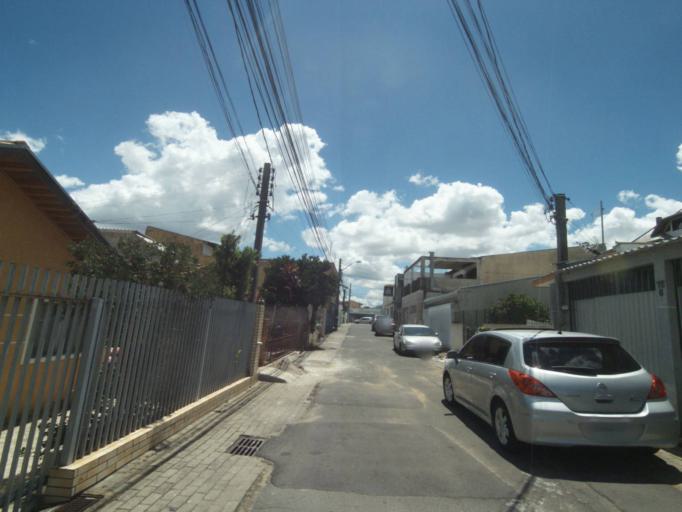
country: BR
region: Parana
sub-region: Curitiba
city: Curitiba
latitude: -25.5061
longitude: -49.3223
